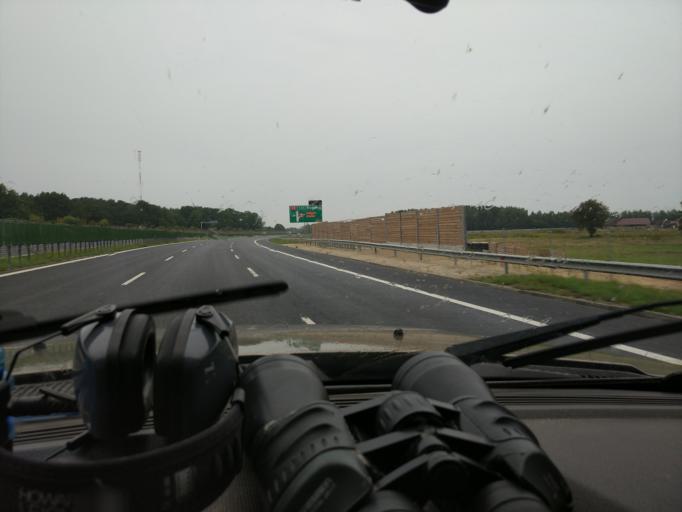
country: PL
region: Masovian Voivodeship
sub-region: Powiat wolominski
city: Slupno
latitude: 52.3447
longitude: 21.1564
